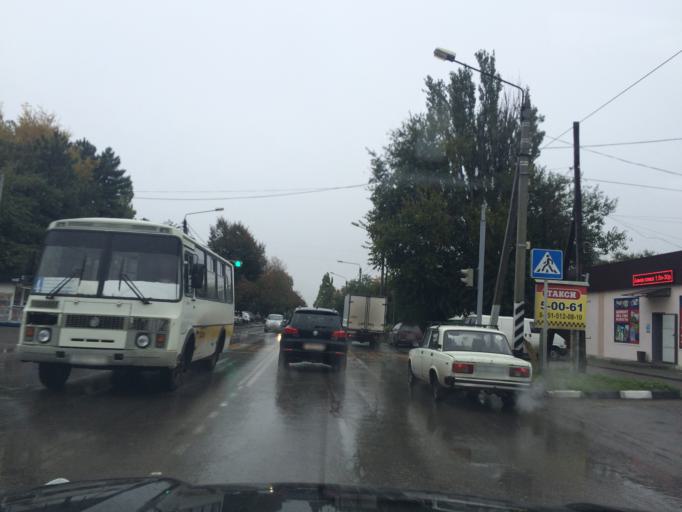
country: RU
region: Rostov
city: Azov
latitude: 47.0945
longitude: 39.4481
